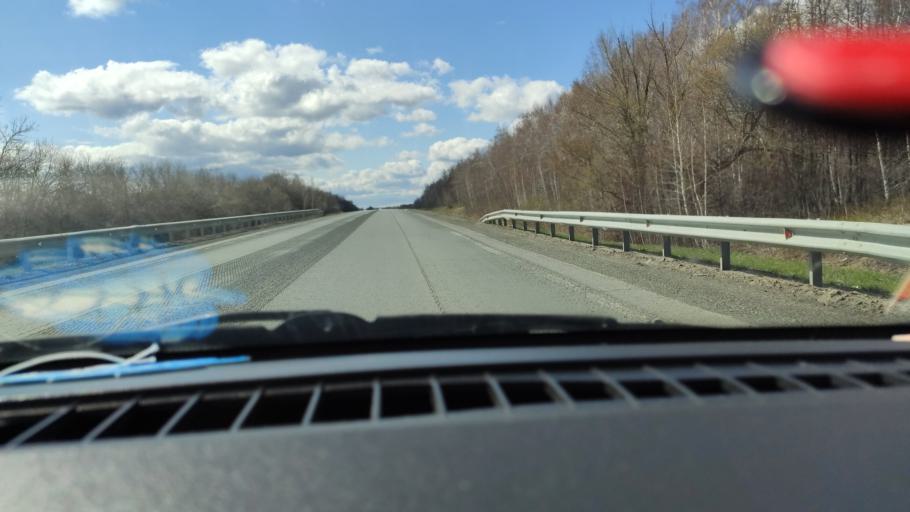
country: RU
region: Saratov
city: Dukhovnitskoye
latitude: 52.6326
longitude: 48.1852
